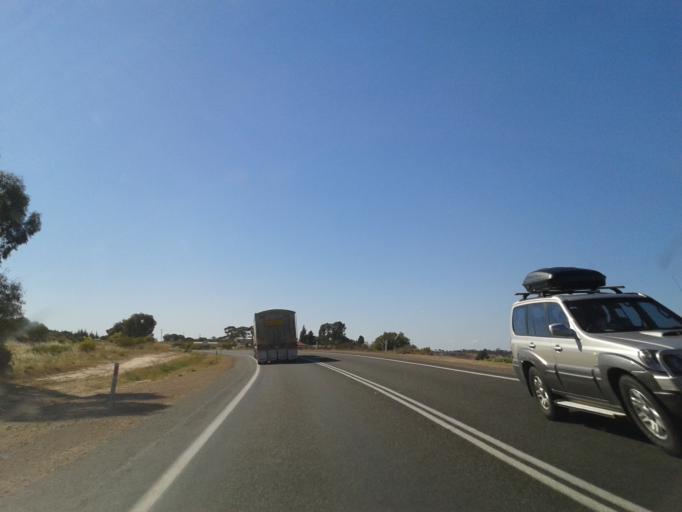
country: AU
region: South Australia
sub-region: Renmark Paringa
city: Renmark
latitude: -34.1858
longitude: 140.7985
